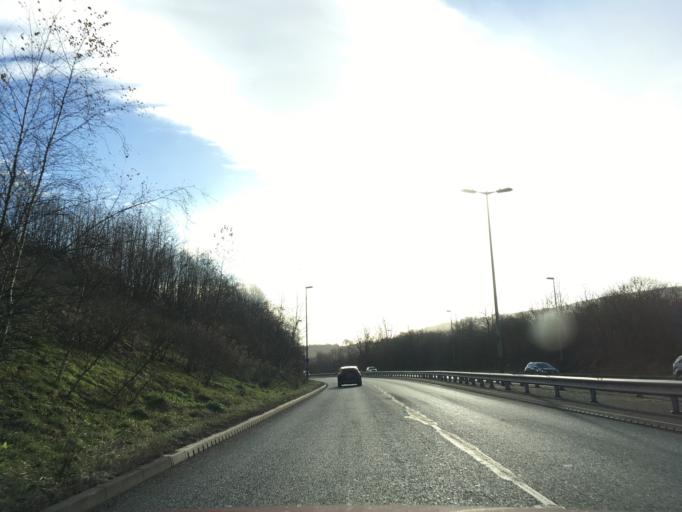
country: GB
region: Wales
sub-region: Caerphilly County Borough
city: Maesycwmmer
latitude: 51.6353
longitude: -3.2313
